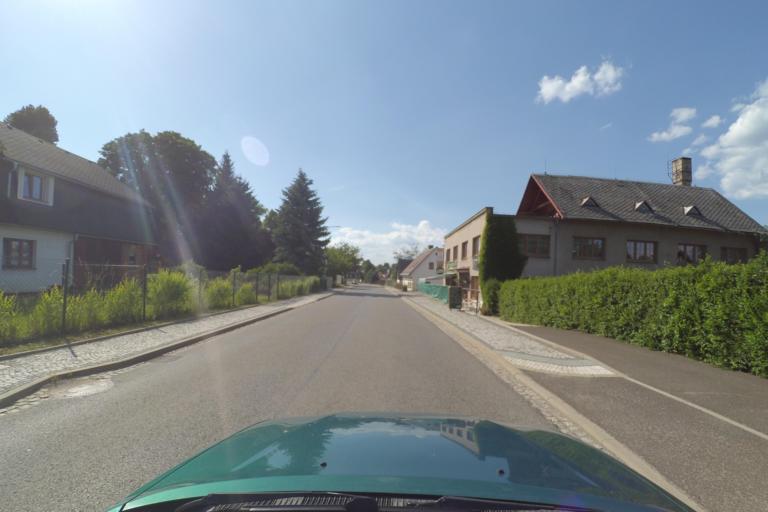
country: CZ
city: Osecna
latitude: 50.6961
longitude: 14.9156
